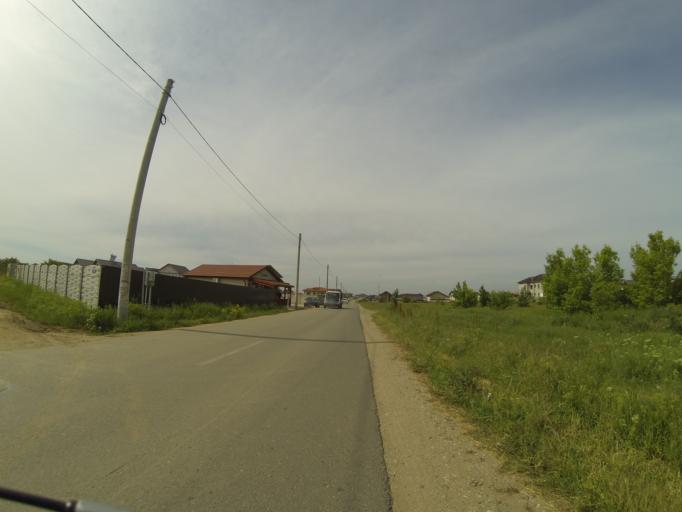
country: RO
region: Dolj
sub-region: Comuna Malu Mare
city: Preajba
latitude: 44.2864
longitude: 23.8481
